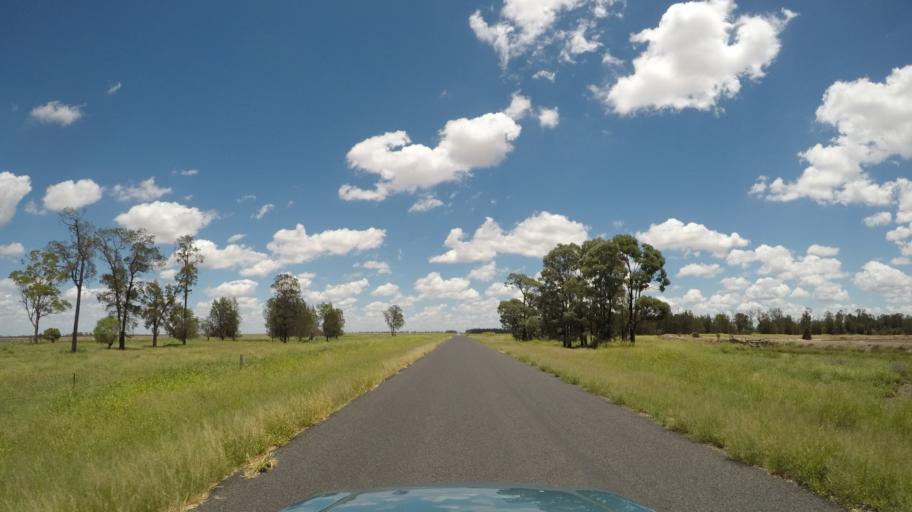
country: AU
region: Queensland
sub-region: Goondiwindi
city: Goondiwindi
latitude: -28.1756
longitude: 150.2542
